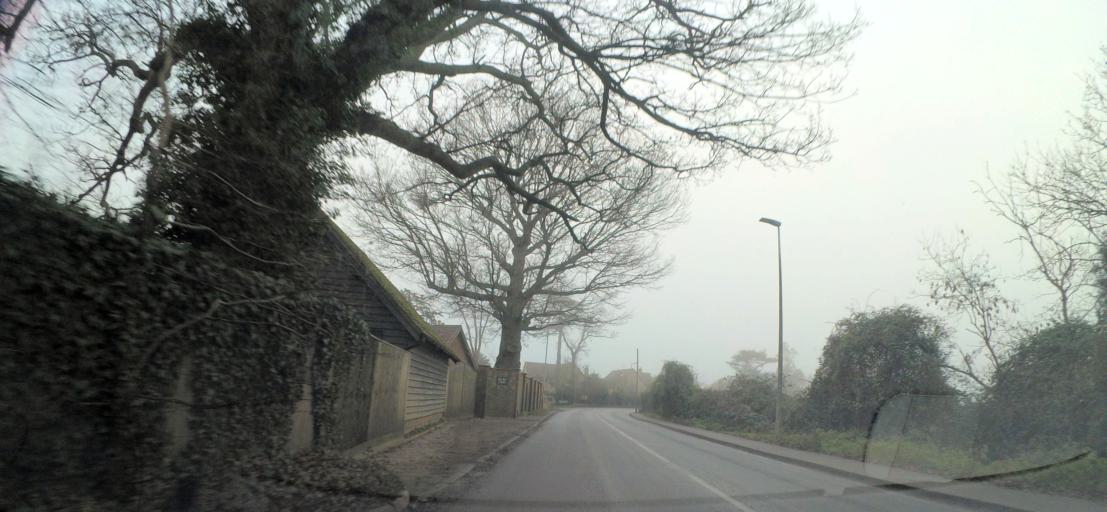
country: GB
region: England
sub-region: West Berkshire
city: Calcot
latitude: 51.4298
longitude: -1.0239
